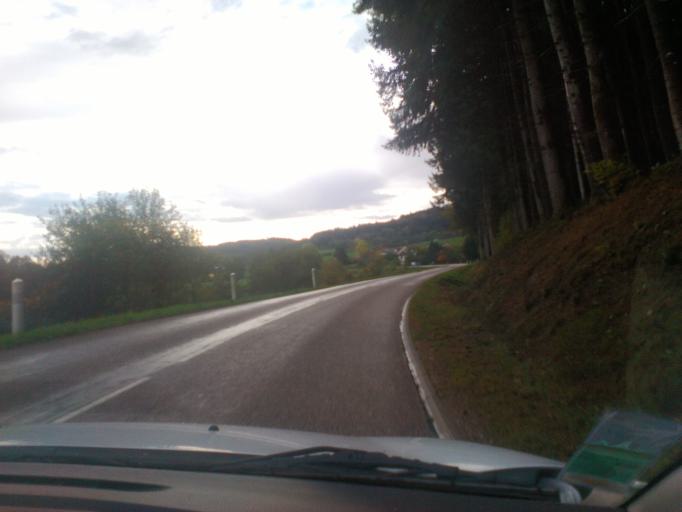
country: FR
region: Lorraine
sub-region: Departement des Vosges
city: Granges-sur-Vologne
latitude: 48.1847
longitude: 6.7977
